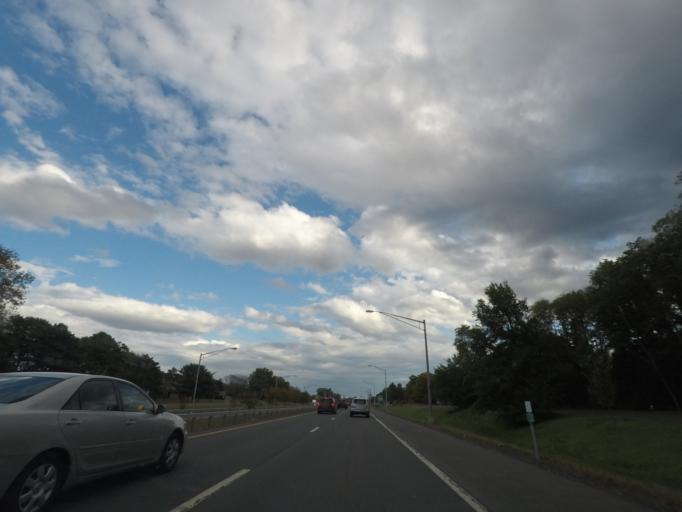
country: US
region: New York
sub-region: Albany County
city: Westmere
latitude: 42.7081
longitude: -73.8638
